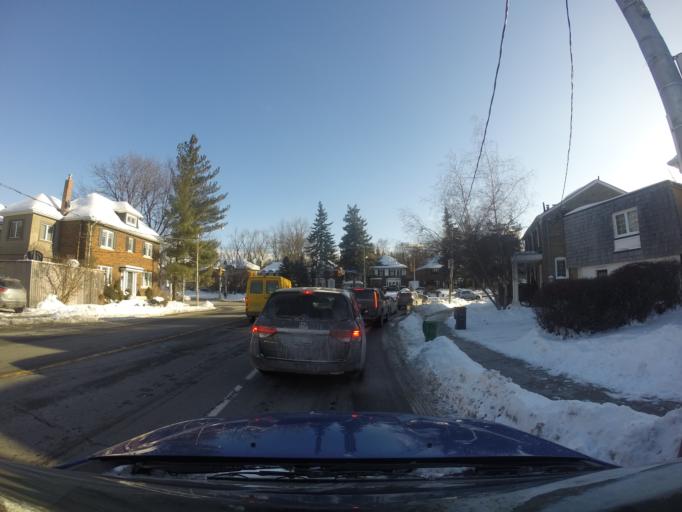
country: CA
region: Ontario
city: Toronto
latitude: 43.7268
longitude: -79.3966
